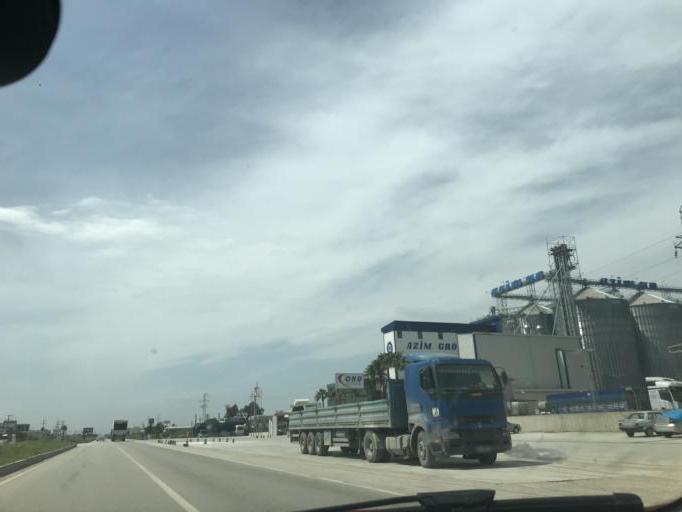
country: TR
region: Adana
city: Yuregir
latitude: 36.9781
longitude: 35.4675
